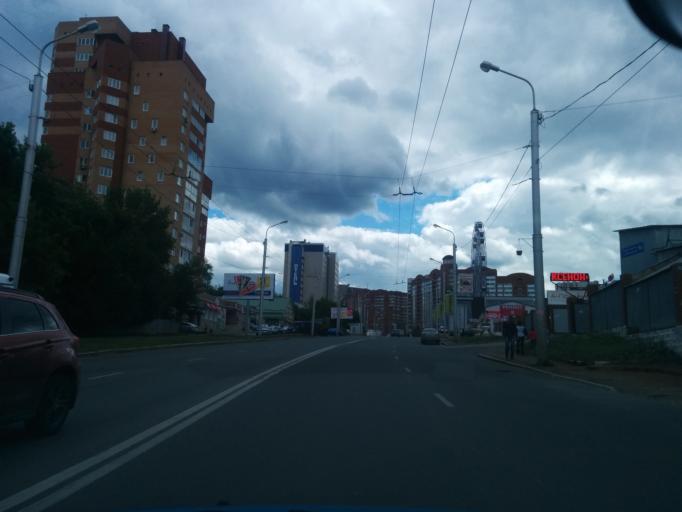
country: RU
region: Bashkortostan
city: Ufa
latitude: 54.7163
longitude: 55.9938
